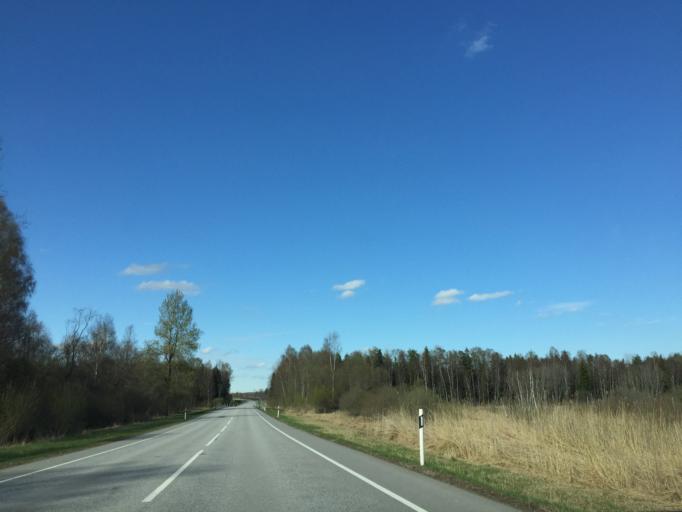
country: EE
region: Vorumaa
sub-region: Antsla vald
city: Vana-Antsla
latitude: 57.8870
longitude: 26.2855
